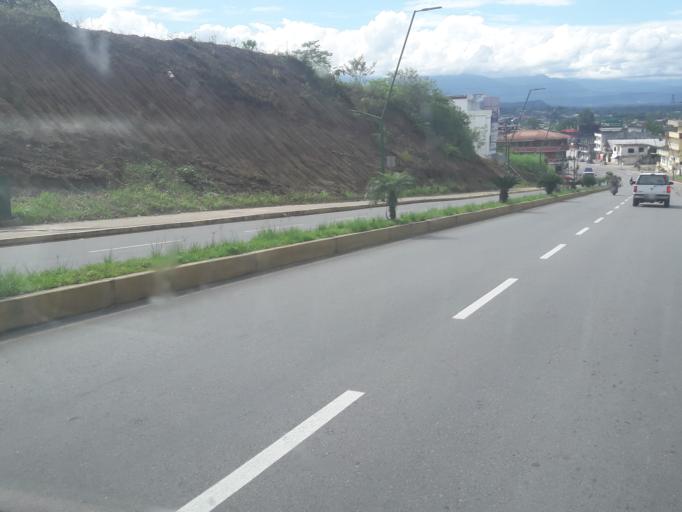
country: EC
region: Napo
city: Tena
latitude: -1.0093
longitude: -77.8094
